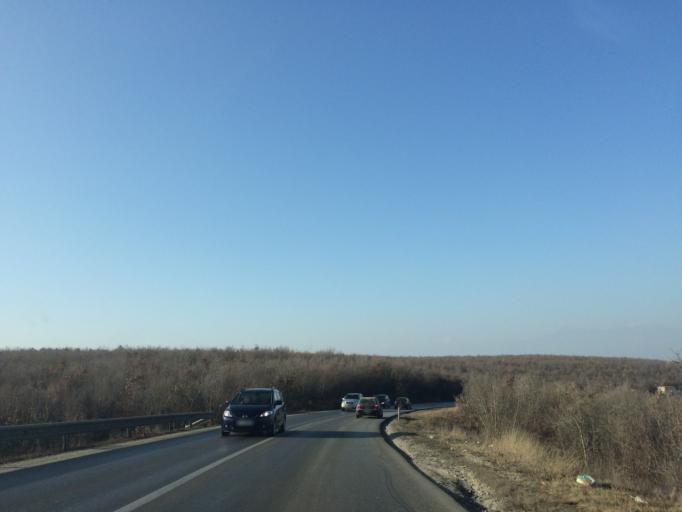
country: XK
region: Pec
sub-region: Komuna e Klines
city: Klina
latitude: 42.5952
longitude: 20.6141
